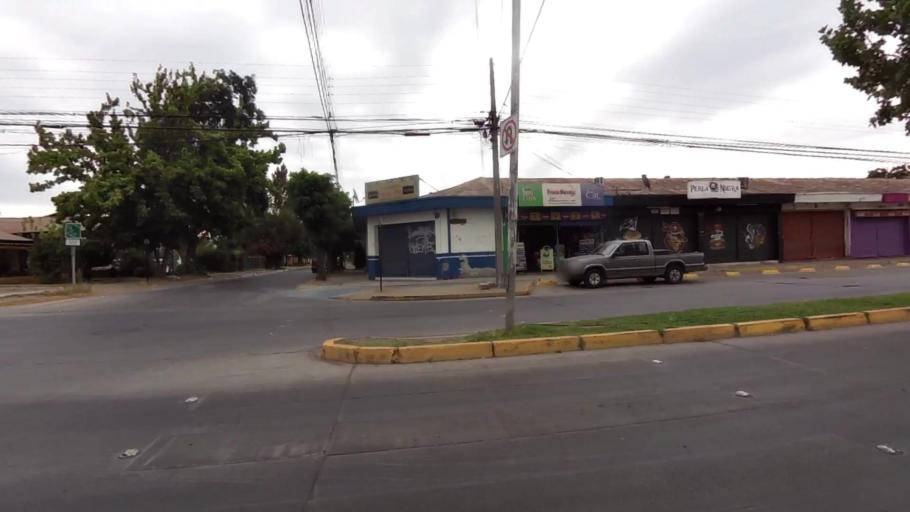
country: CL
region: O'Higgins
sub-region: Provincia de Cachapoal
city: Rancagua
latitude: -34.1640
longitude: -70.7339
